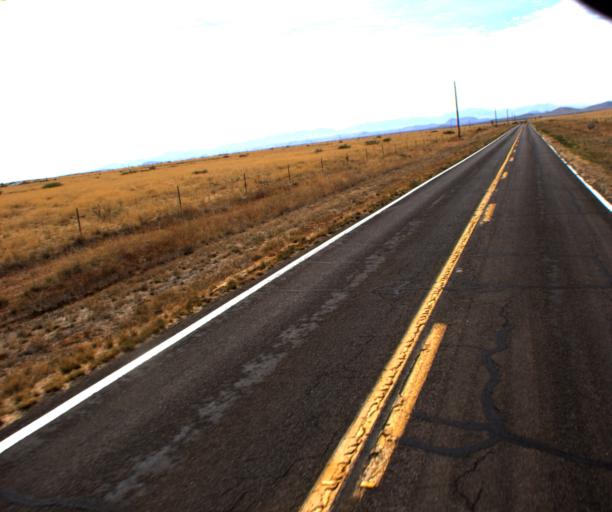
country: US
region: Arizona
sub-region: Cochise County
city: Willcox
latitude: 31.9923
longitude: -109.4418
